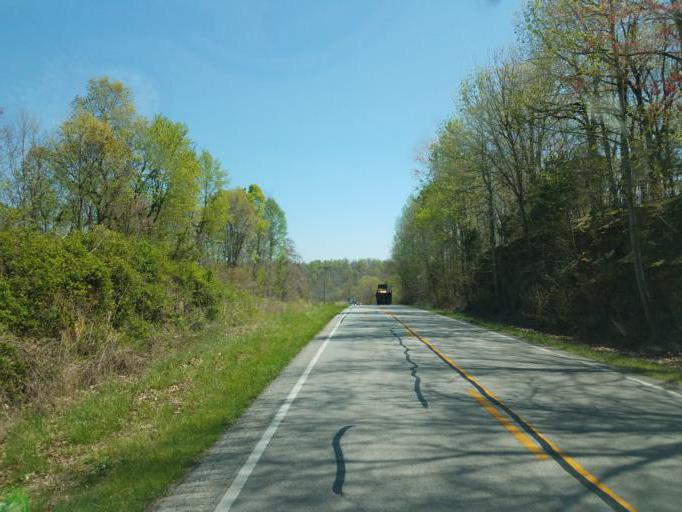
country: US
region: Kentucky
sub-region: Barren County
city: Cave City
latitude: 37.1331
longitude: -86.0119
